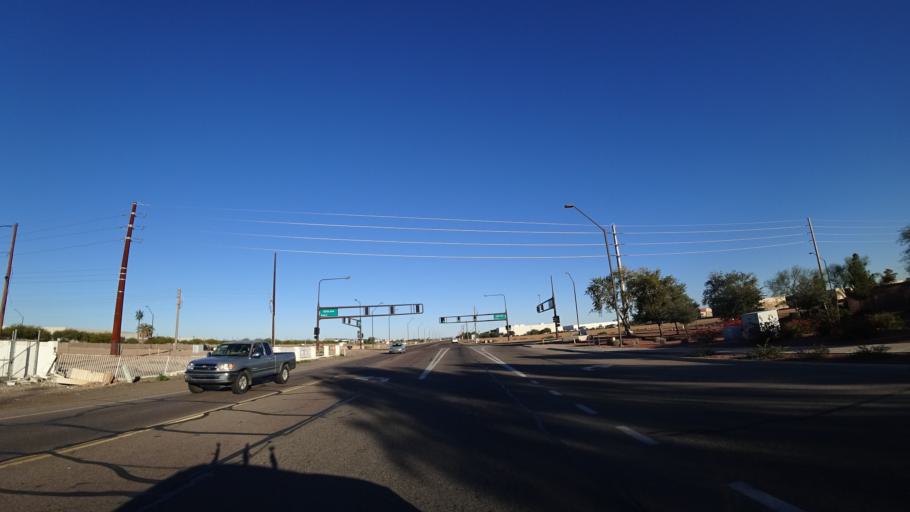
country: US
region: Arizona
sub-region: Maricopa County
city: Tolleson
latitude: 33.4499
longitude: -112.2908
